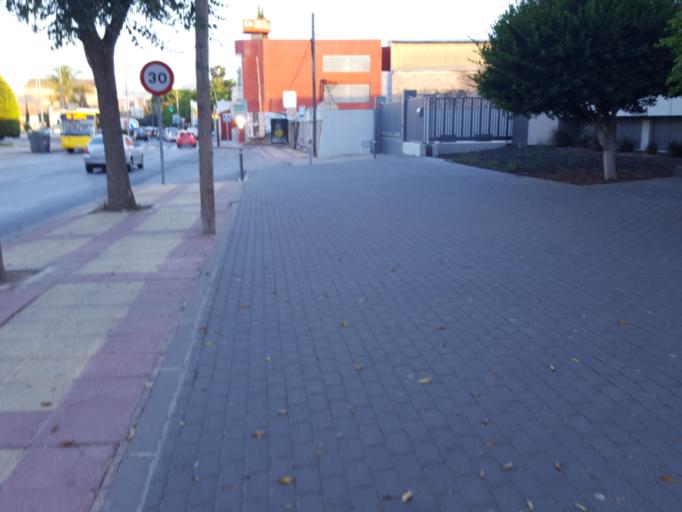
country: ES
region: Murcia
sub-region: Murcia
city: Murcia
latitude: 38.0042
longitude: -1.1477
